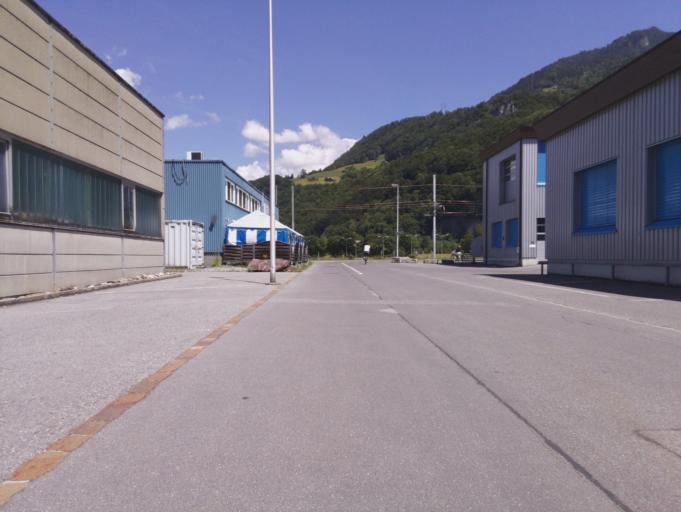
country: CH
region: Glarus
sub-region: Glarus
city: Nafels
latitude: 47.1075
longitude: 9.0679
